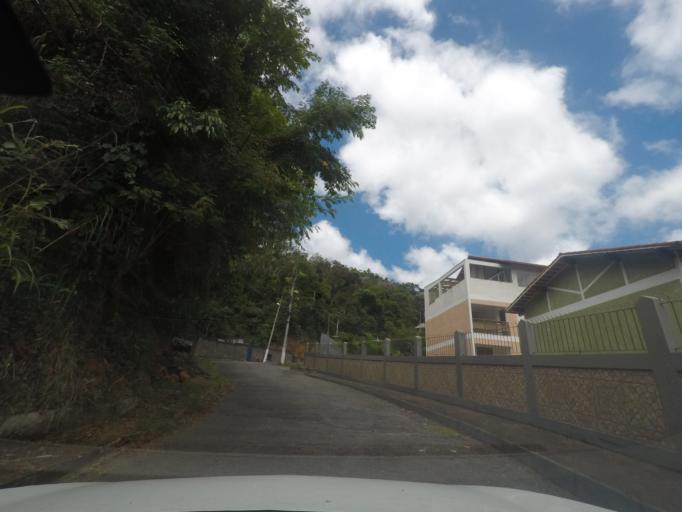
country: BR
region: Rio de Janeiro
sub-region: Teresopolis
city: Teresopolis
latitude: -22.4053
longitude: -42.9821
